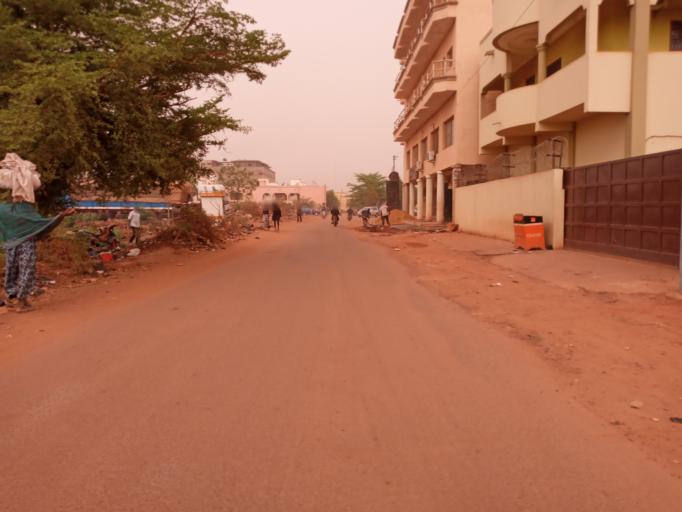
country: ML
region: Bamako
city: Bamako
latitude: 12.6526
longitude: -7.9358
